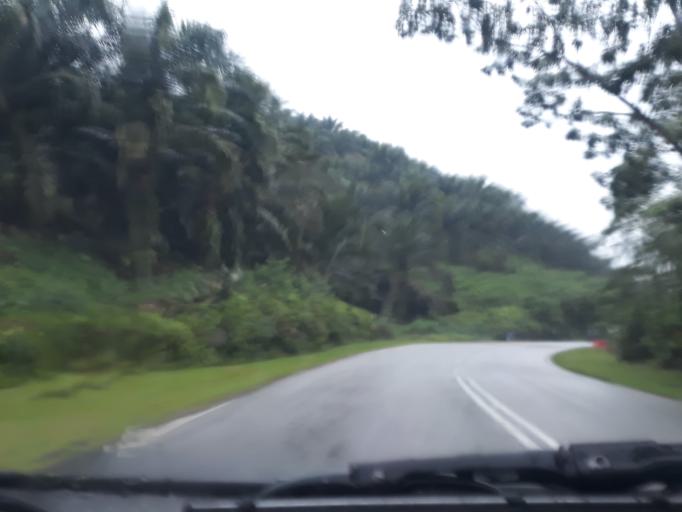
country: MY
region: Kedah
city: Kulim
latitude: 5.3432
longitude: 100.5869
